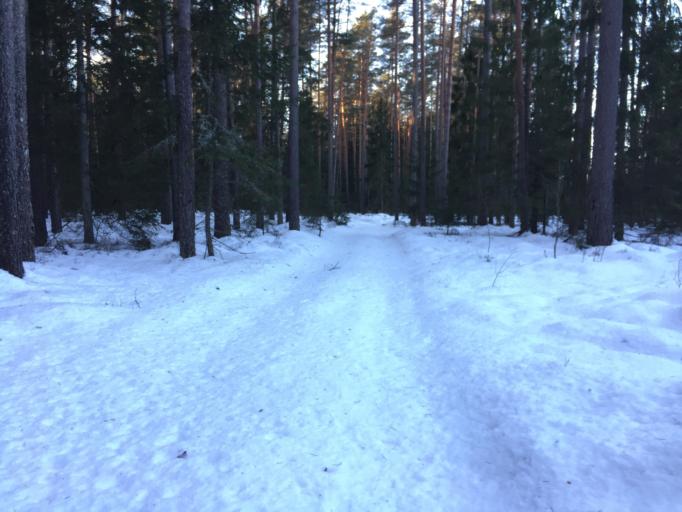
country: LV
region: Kegums
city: Kegums
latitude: 56.7335
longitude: 24.6487
